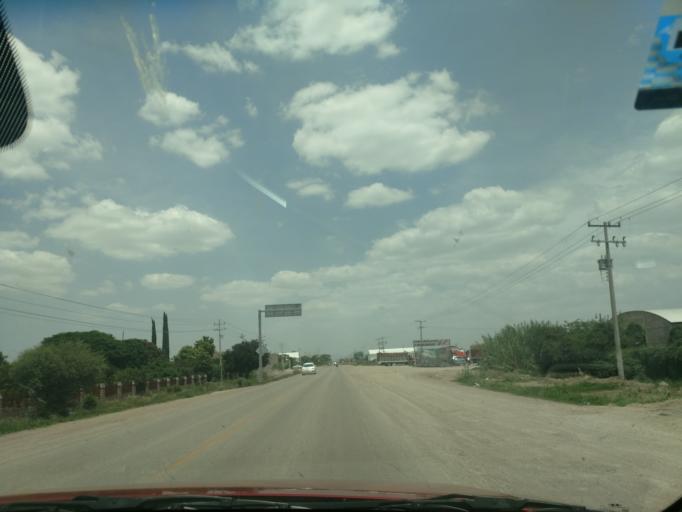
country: MX
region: San Luis Potosi
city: Ciudad Fernandez
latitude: 21.9460
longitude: -100.0524
